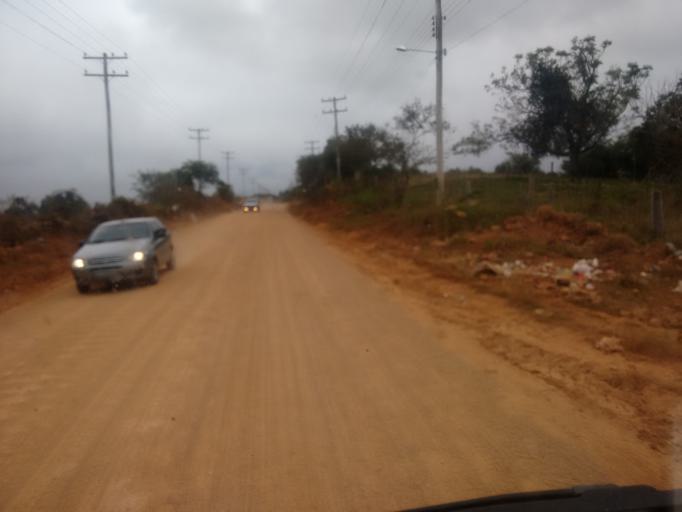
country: BR
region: Rio Grande do Sul
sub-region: Camaqua
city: Camaqua
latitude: -30.8332
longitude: -51.8201
